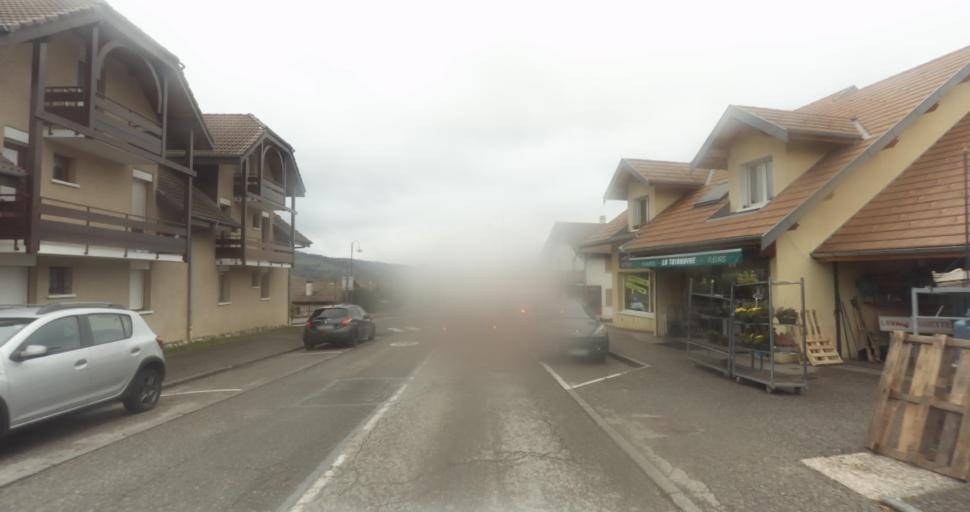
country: FR
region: Rhone-Alpes
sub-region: Departement de la Haute-Savoie
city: Thorens-Glieres
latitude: 45.9965
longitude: 6.2445
